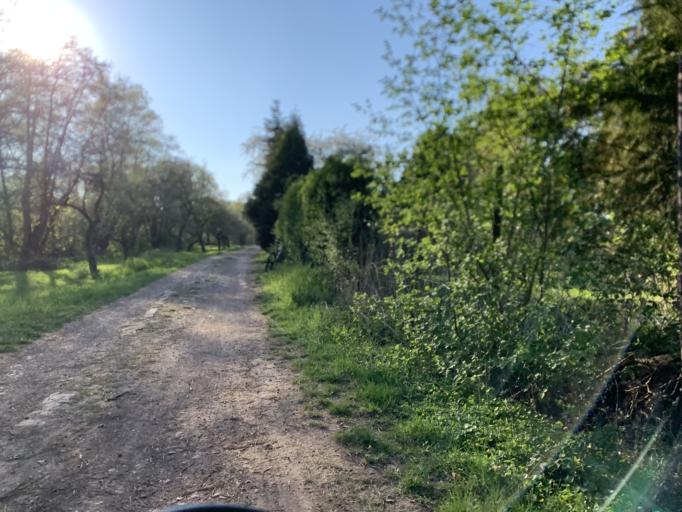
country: DE
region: Rheinland-Pfalz
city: Hargesheim
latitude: 49.8862
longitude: 7.8555
